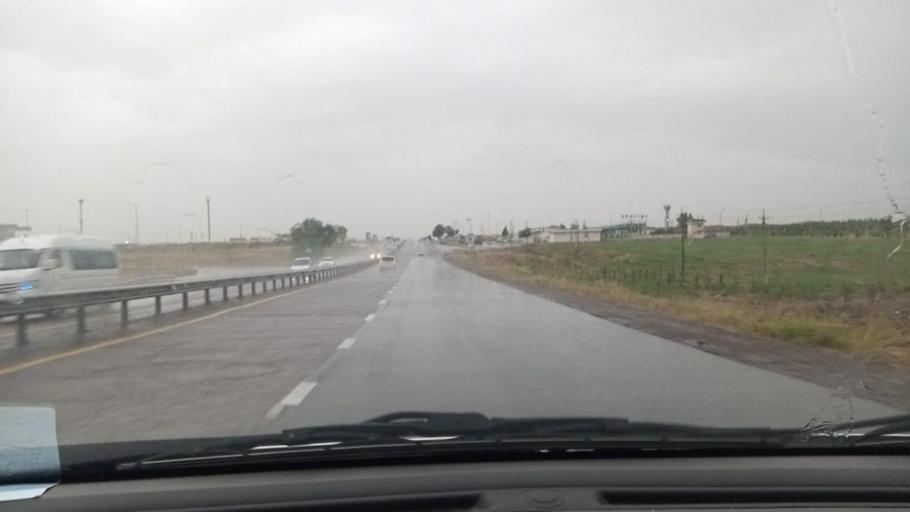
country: UZ
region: Toshkent
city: Ohangaron
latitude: 40.9449
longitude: 69.5773
